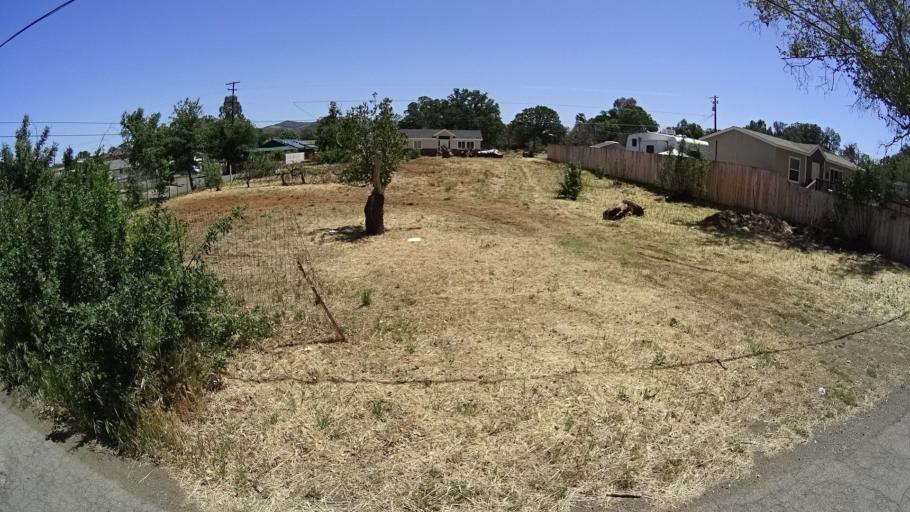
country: US
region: California
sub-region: Lake County
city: Lower Lake
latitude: 38.9116
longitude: -122.6060
